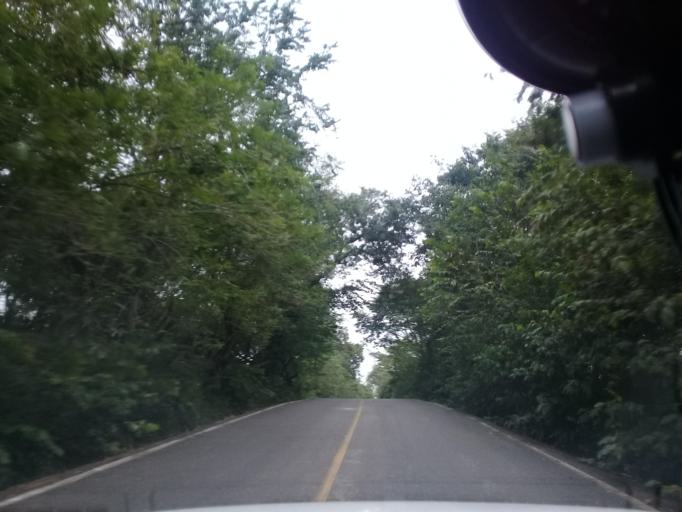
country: MX
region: Veracruz
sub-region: Chalma
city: San Pedro Coyutla
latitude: 21.2087
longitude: -98.4188
